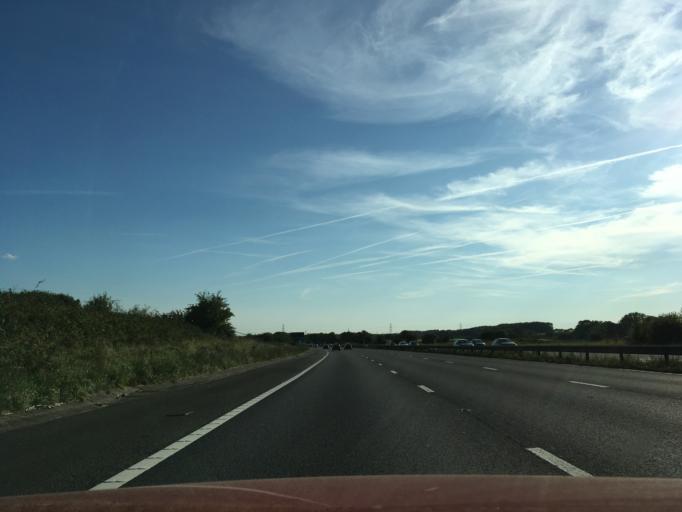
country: GB
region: England
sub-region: South Gloucestershire
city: Alveston
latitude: 51.5729
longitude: -2.5238
